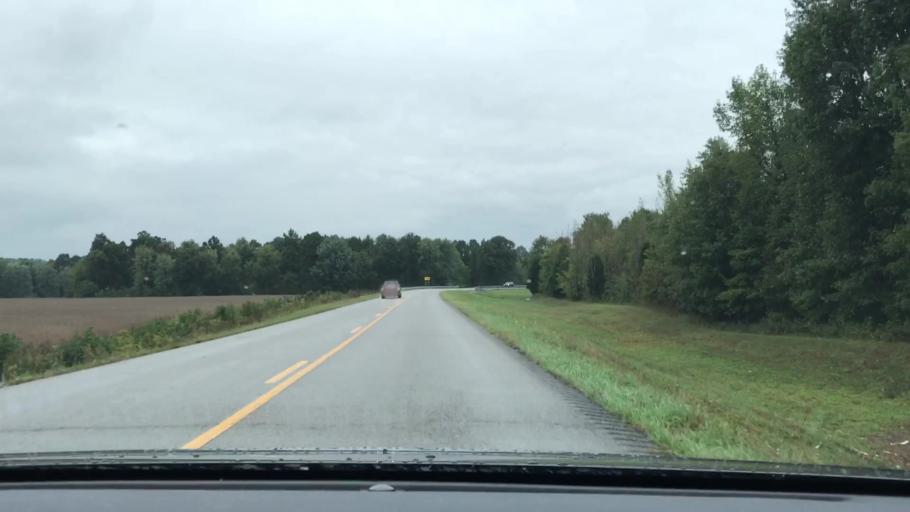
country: US
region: Kentucky
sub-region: McLean County
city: Calhoun
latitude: 37.4929
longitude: -87.2456
